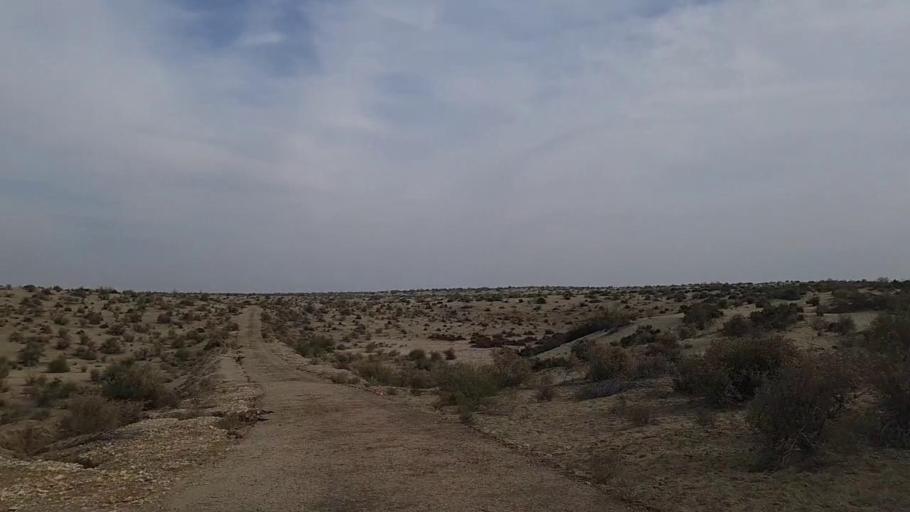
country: PK
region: Sindh
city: Jam Sahib
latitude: 26.4573
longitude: 68.6467
